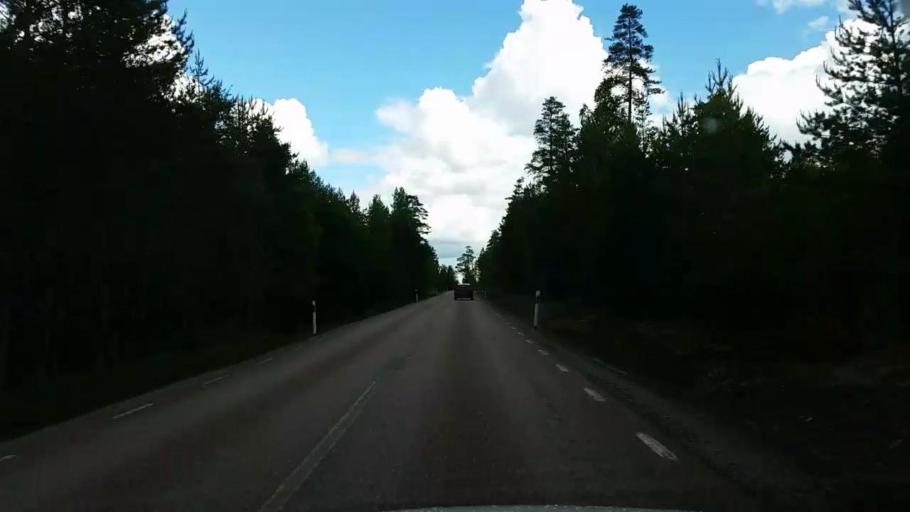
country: SE
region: Vaestmanland
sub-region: Fagersta Kommun
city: Fagersta
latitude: 59.8650
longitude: 15.8422
